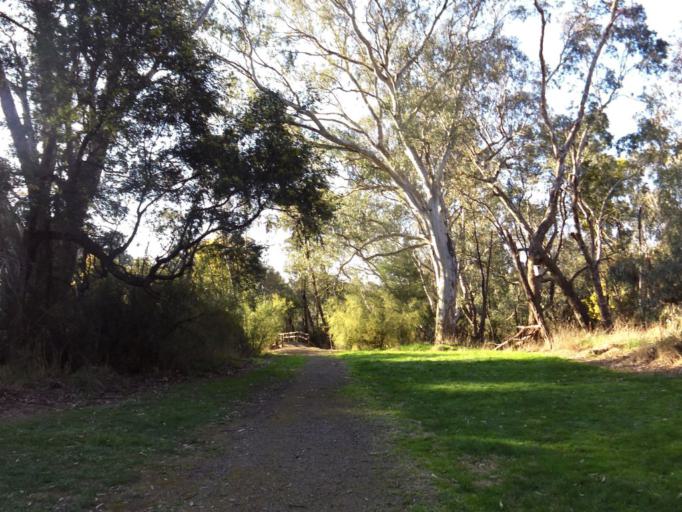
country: AU
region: Victoria
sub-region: Murrindindi
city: Alexandra
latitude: -37.2087
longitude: 145.4284
